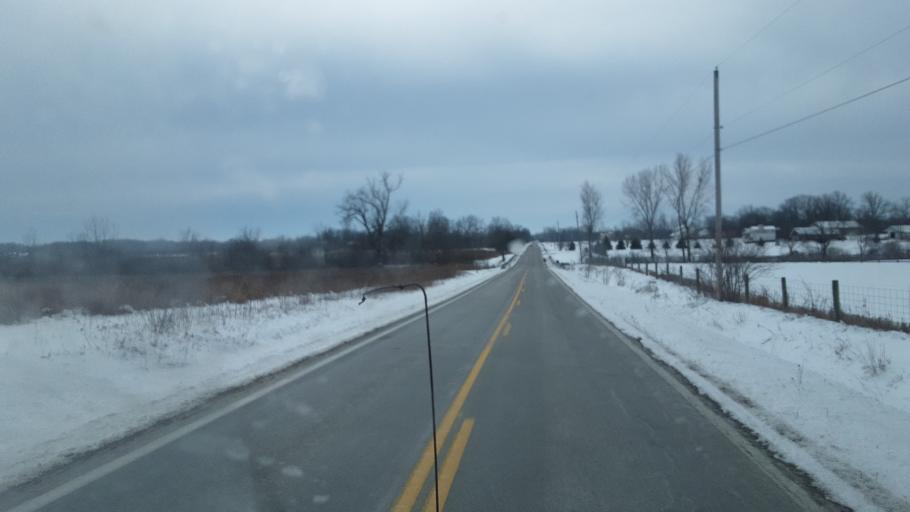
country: US
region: Ohio
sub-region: Madison County
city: Choctaw Lake
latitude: 39.9671
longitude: -83.5027
